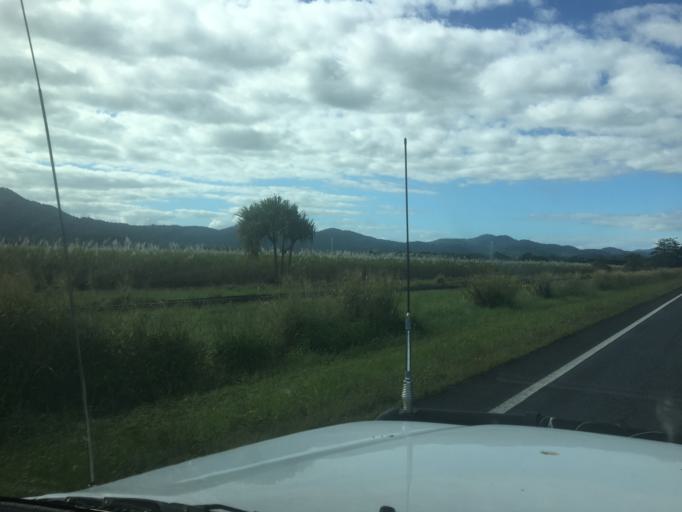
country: AU
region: Queensland
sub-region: Cassowary Coast
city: Innisfail
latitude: -17.2911
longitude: 145.9255
